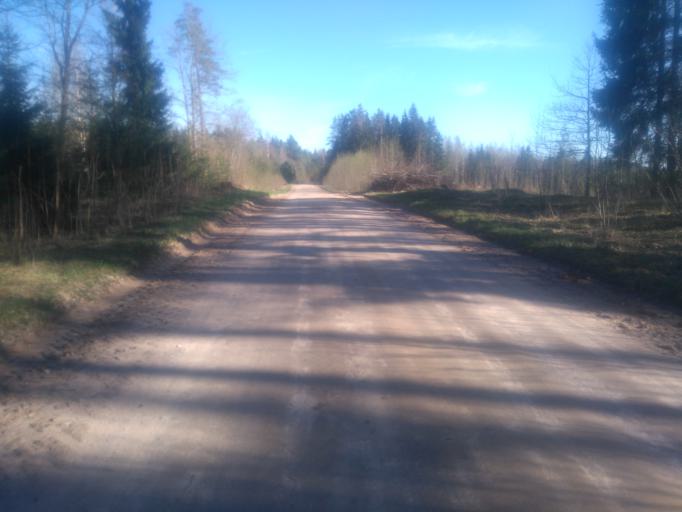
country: LV
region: Vecpiebalga
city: Vecpiebalga
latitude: 57.0139
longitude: 25.8373
